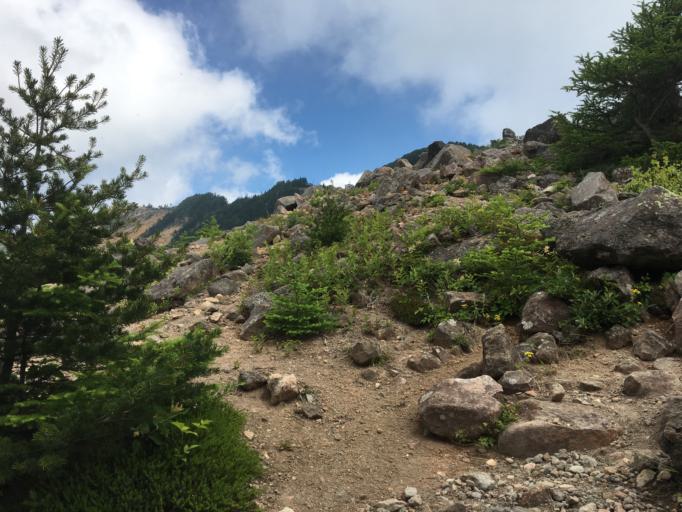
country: JP
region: Nagano
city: Komoro
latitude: 36.4167
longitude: 138.4579
